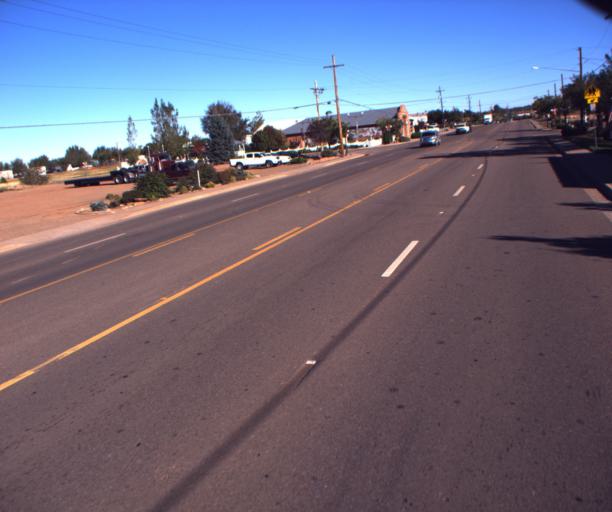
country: US
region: Arizona
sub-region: Navajo County
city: Taylor
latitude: 34.4643
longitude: -110.0911
